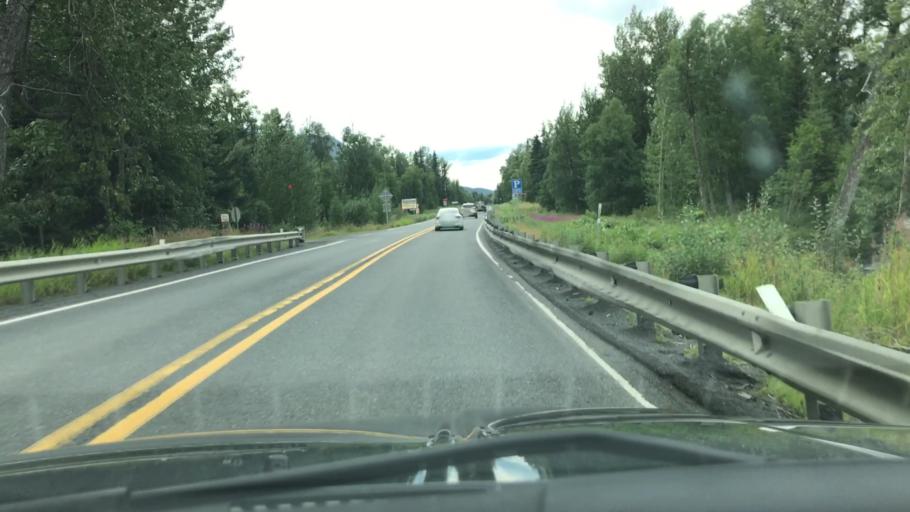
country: US
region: Alaska
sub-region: Kenai Peninsula Borough
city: Seward
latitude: 60.4840
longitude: -149.8814
